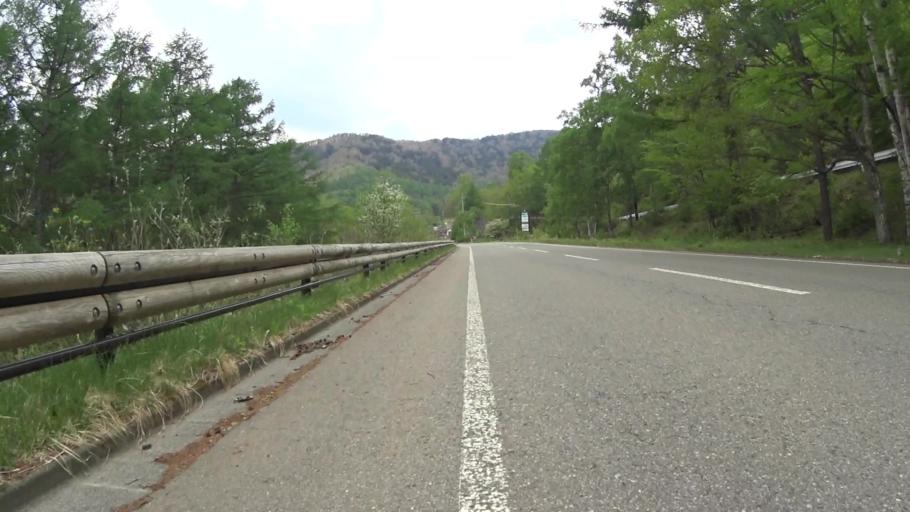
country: JP
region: Nagano
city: Saku
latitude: 36.0731
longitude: 138.3817
